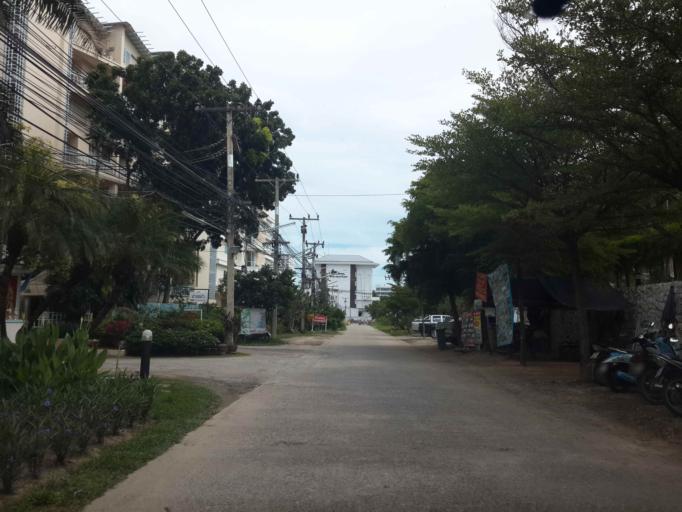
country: TH
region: Prachuap Khiri Khan
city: Hua Hin
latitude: 12.5330
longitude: 99.9681
